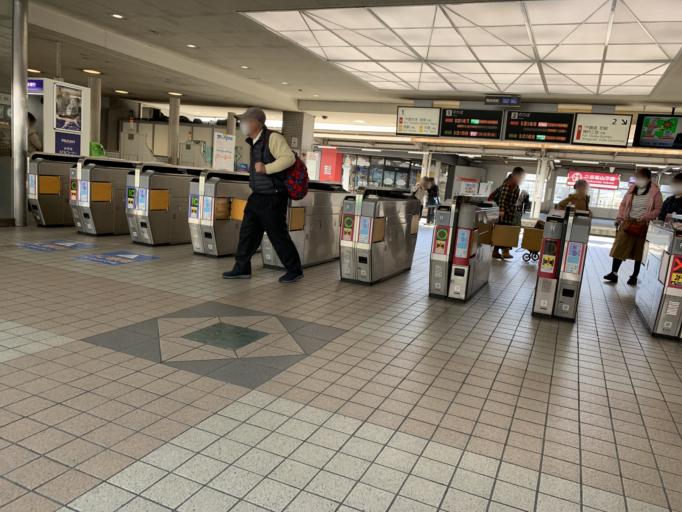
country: JP
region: Nara
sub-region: Ikoma-shi
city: Ikoma
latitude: 34.6978
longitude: 135.7506
